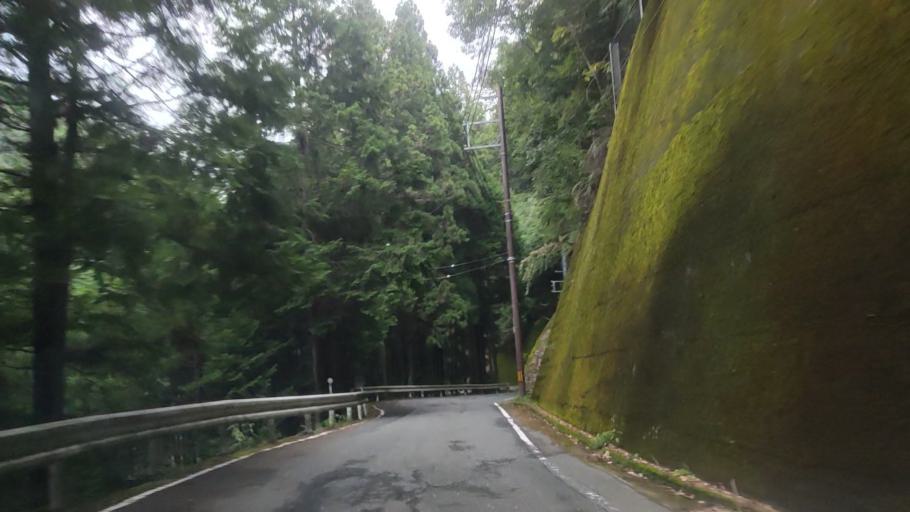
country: JP
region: Wakayama
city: Koya
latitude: 34.2399
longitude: 135.6523
